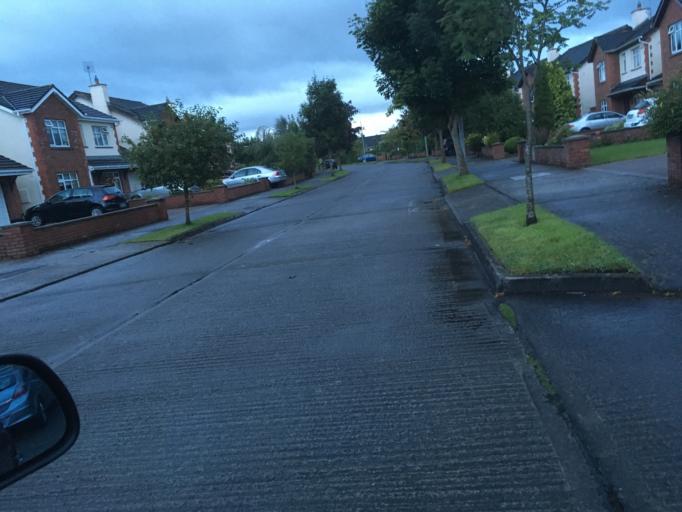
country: IE
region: Leinster
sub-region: Kildare
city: Droichead Nua
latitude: 53.1817
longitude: -6.7838
